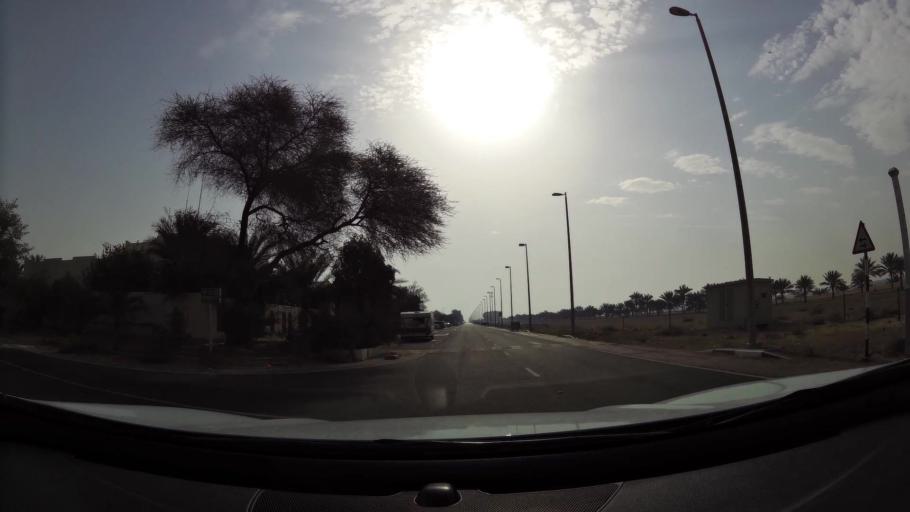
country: AE
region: Abu Dhabi
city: Abu Dhabi
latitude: 24.2420
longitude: 54.7128
